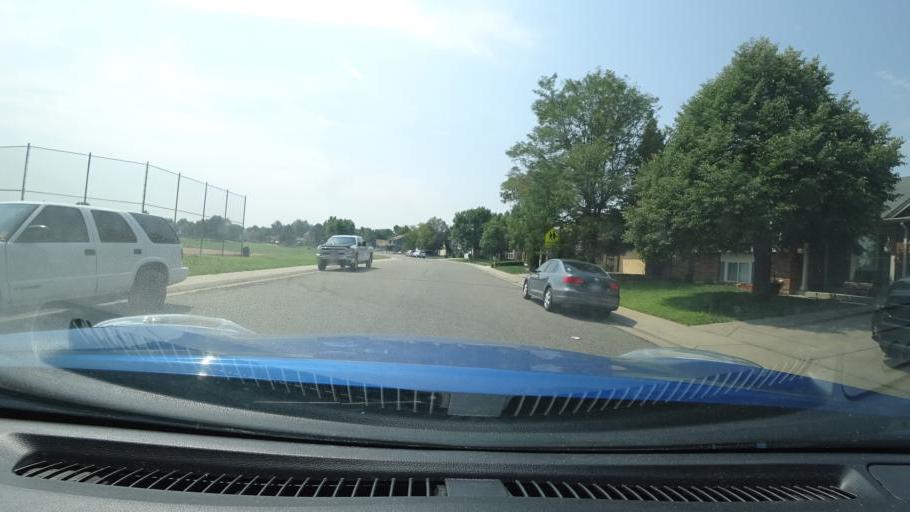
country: US
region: Colorado
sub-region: Adams County
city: Aurora
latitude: 39.7816
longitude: -104.7633
